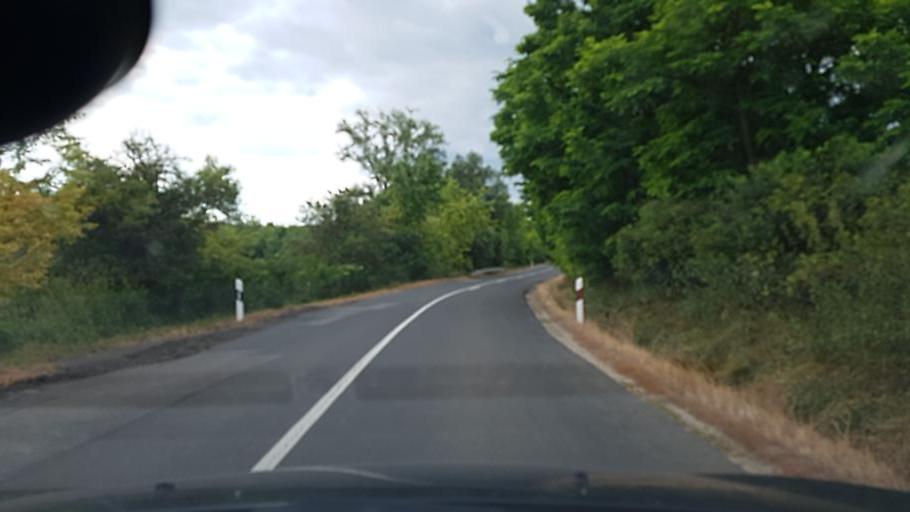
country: HU
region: Pest
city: Piliscsaba
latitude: 47.6424
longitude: 18.7836
